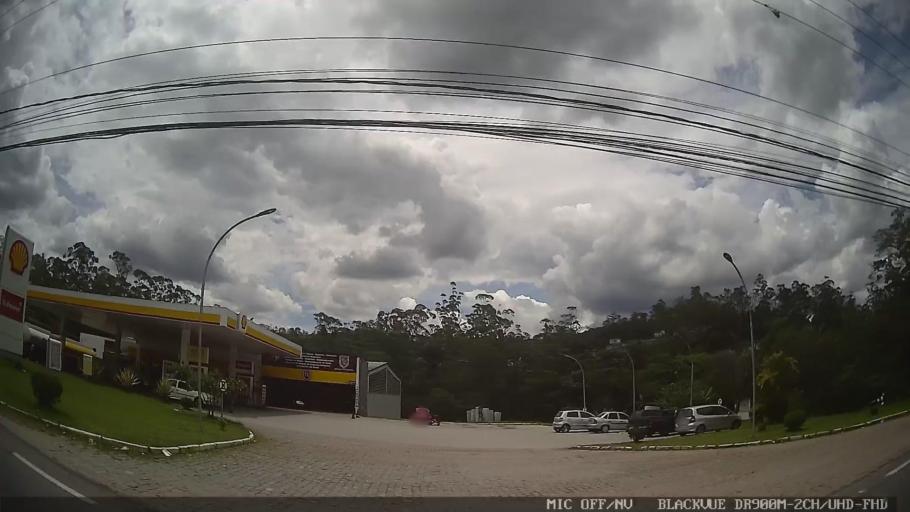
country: BR
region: Sao Paulo
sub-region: Ribeirao Pires
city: Ribeirao Pires
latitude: -23.6826
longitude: -46.3670
